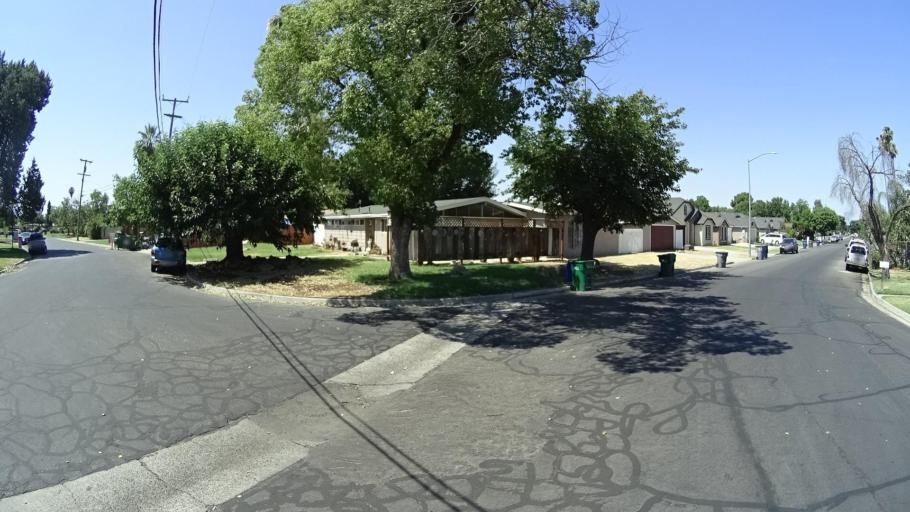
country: US
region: California
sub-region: Fresno County
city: Sunnyside
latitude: 36.7559
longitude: -119.7133
